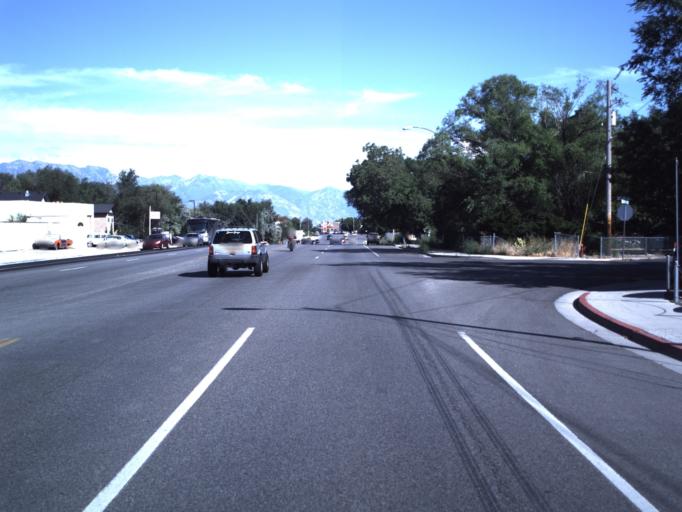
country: US
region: Utah
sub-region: Utah County
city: Lehi
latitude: 40.4006
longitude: -111.8530
